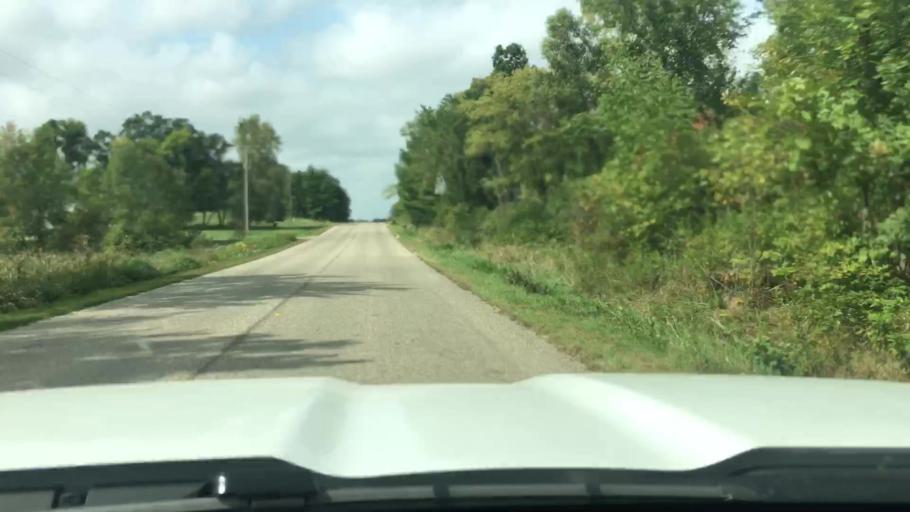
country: US
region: Michigan
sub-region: Eaton County
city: Dimondale
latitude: 42.6257
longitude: -84.6891
